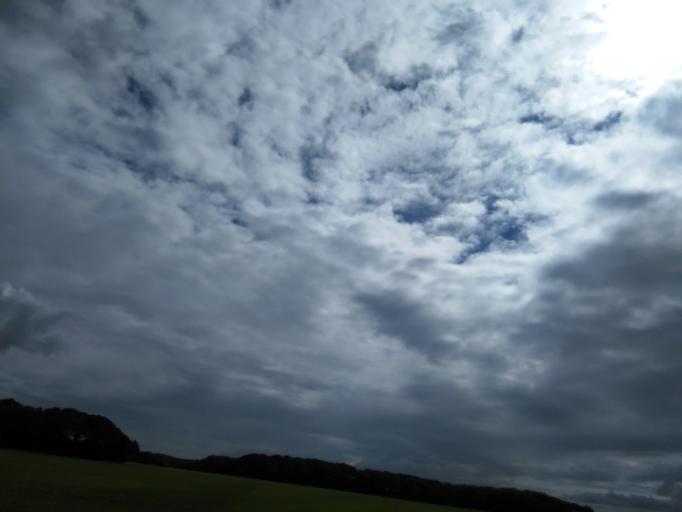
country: DK
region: Central Jutland
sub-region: Odder Kommune
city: Odder
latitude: 55.8715
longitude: 10.1473
